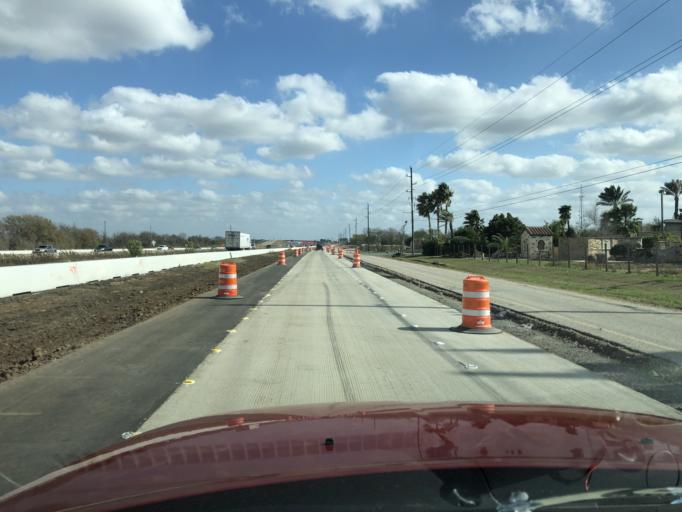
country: US
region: Texas
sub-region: Austin County
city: Sealy
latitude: 29.7746
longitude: -96.0865
